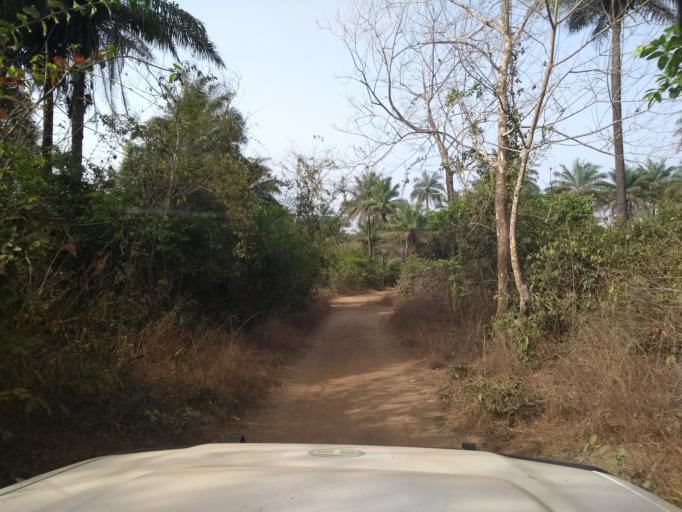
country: GN
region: Kindia
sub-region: Prefecture de Dubreka
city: Dubreka
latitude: 9.8180
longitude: -13.5568
